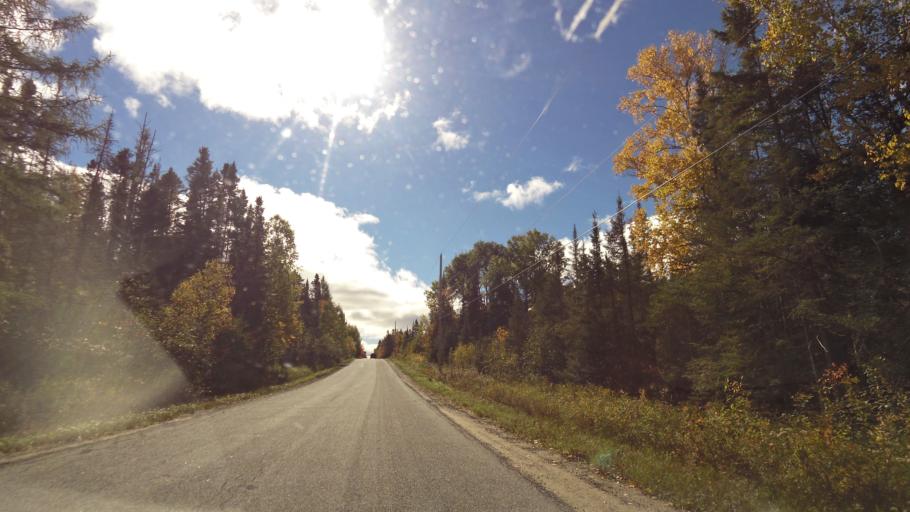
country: CA
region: Ontario
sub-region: Nipissing District
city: North Bay
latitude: 46.3638
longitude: -79.4872
